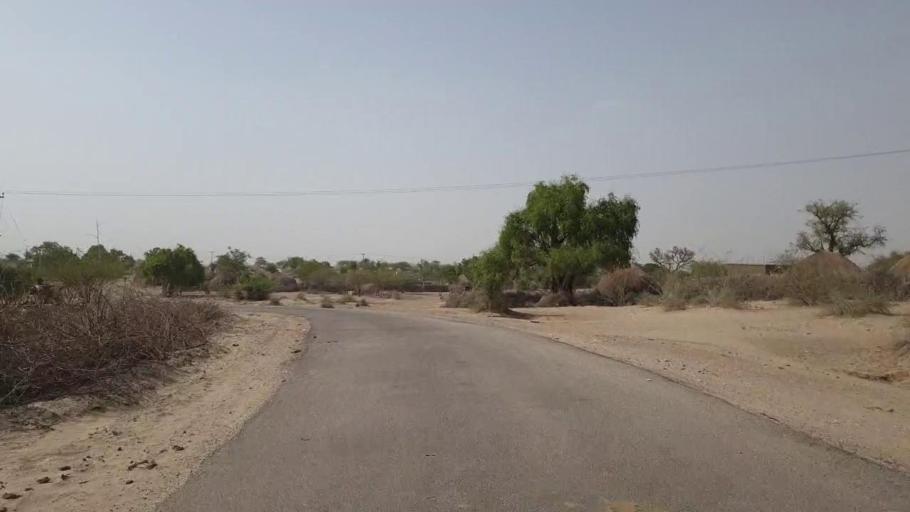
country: PK
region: Sindh
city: Mithi
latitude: 24.6106
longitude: 69.9207
